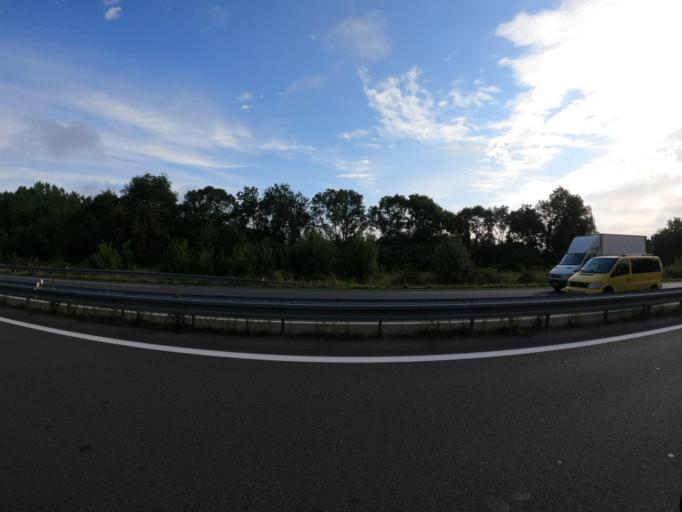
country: FR
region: Pays de la Loire
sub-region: Departement de Maine-et-Loire
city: Allonnes
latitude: 47.2913
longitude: -0.0138
